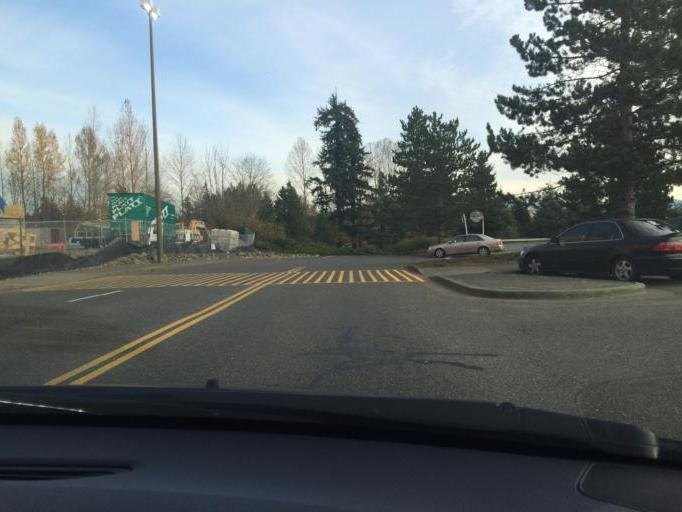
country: US
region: Washington
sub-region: Whatcom County
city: Bellingham
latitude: 48.7878
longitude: -122.4885
